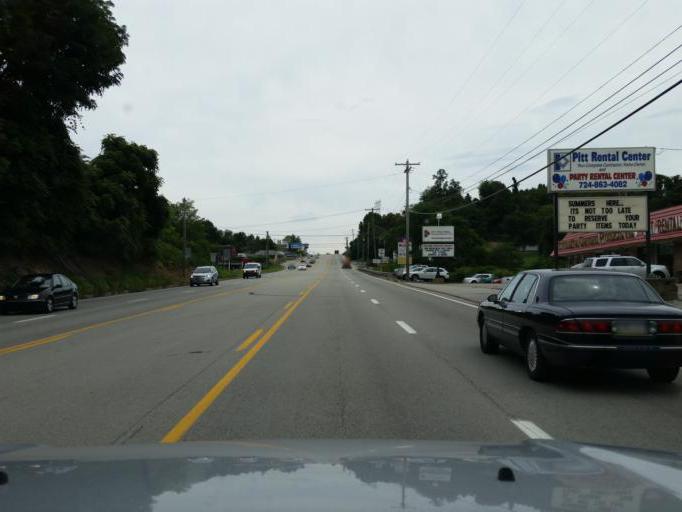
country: US
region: Pennsylvania
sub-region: Westmoreland County
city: Manor
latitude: 40.3131
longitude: -79.6688
